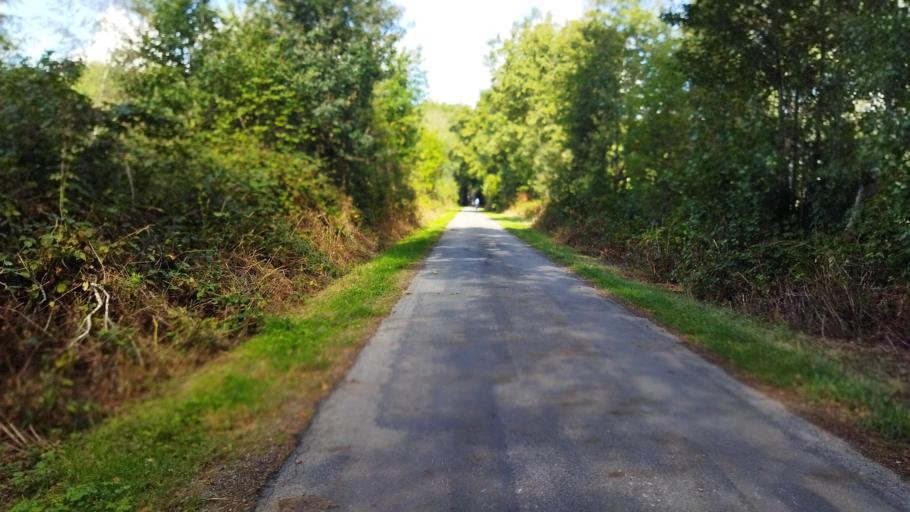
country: DE
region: Lower Saxony
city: Salzbergen
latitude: 52.3406
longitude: 7.3449
